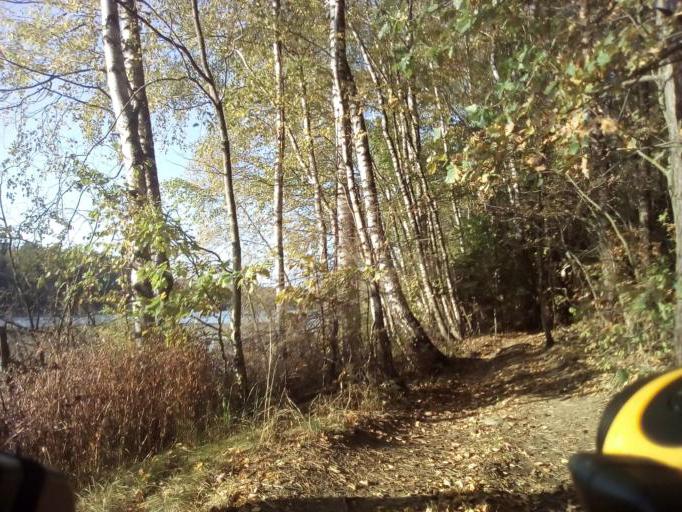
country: RU
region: Moskovskaya
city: Gzhel'
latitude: 55.5829
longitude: 38.3257
